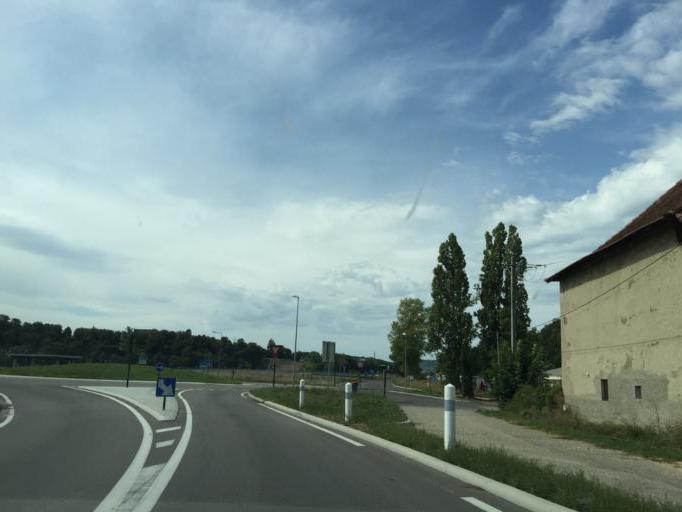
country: FR
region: Rhone-Alpes
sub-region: Departement de l'Isere
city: Saint-Didier-de-la-Tour
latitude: 45.5575
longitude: 5.4676
